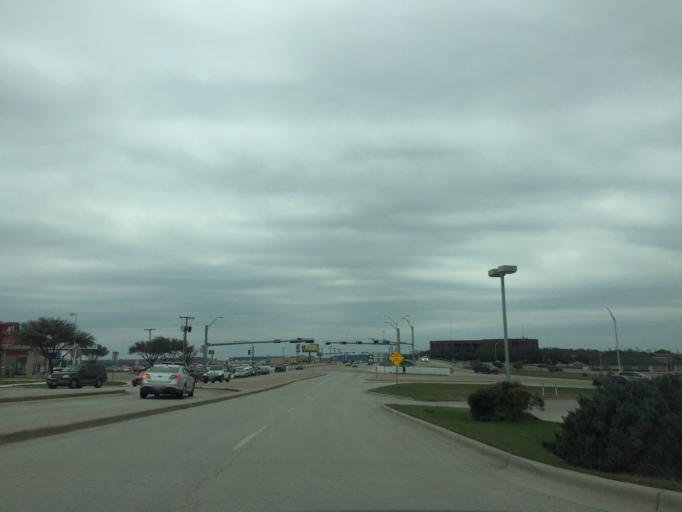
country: US
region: Texas
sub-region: Bell County
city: Harker Heights
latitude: 31.0726
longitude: -97.6713
